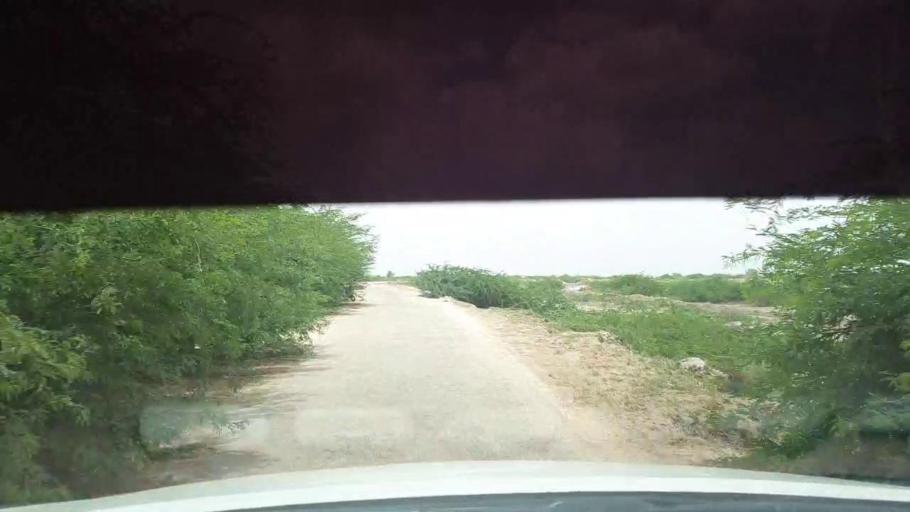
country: PK
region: Sindh
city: Kadhan
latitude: 24.4829
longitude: 69.0665
